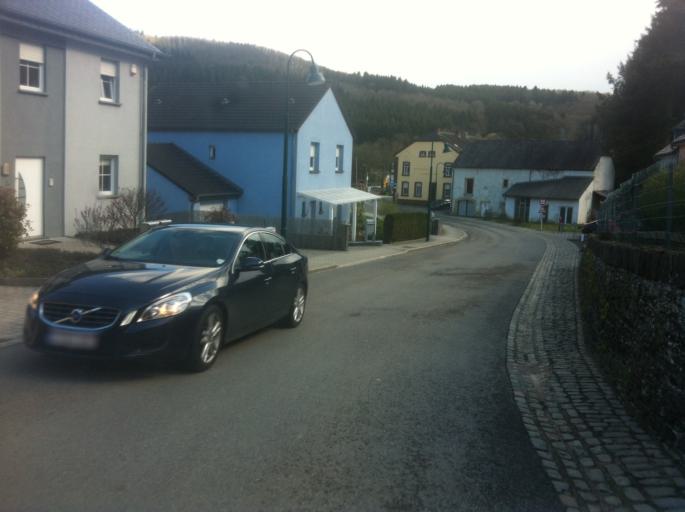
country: LU
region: Diekirch
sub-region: Canton de Wiltz
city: Wilwerwiltz
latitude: 50.0179
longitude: 6.0061
